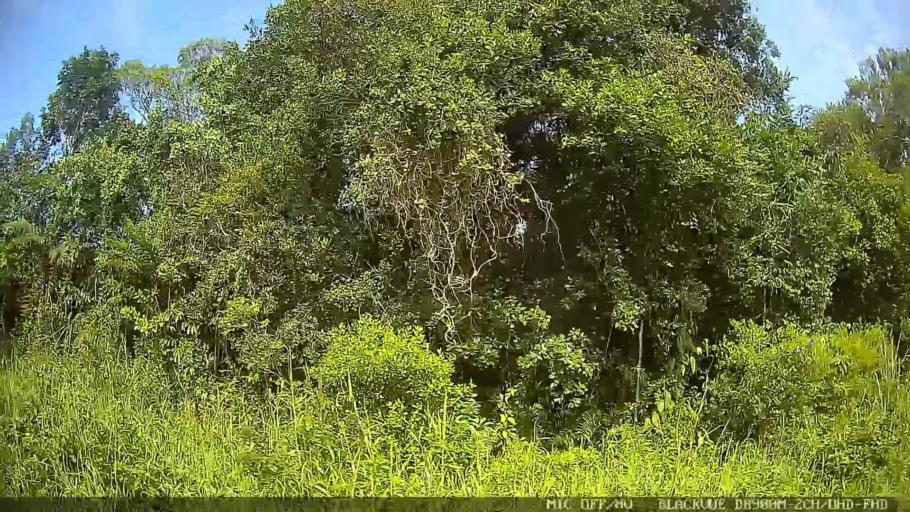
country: BR
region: Sao Paulo
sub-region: Peruibe
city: Peruibe
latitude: -24.2275
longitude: -46.9152
